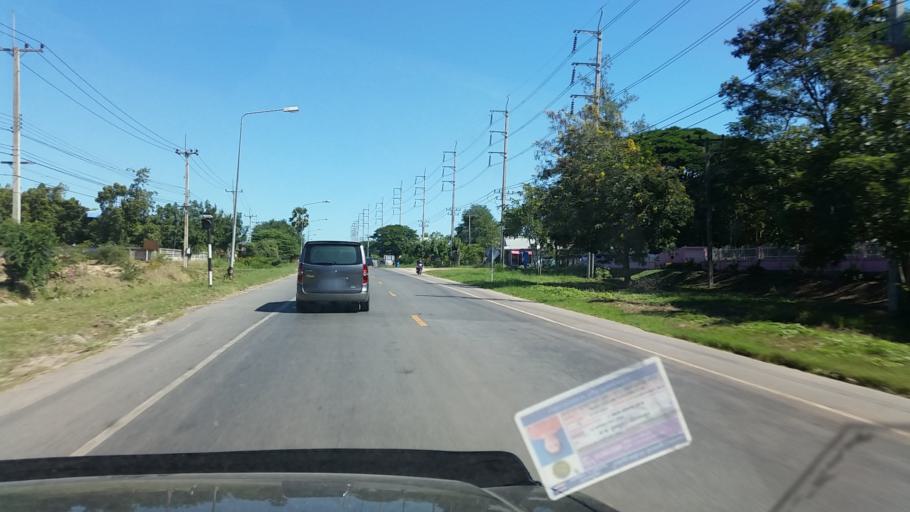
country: TH
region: Chaiyaphum
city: Ban Khwao
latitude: 15.7835
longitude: 101.9501
